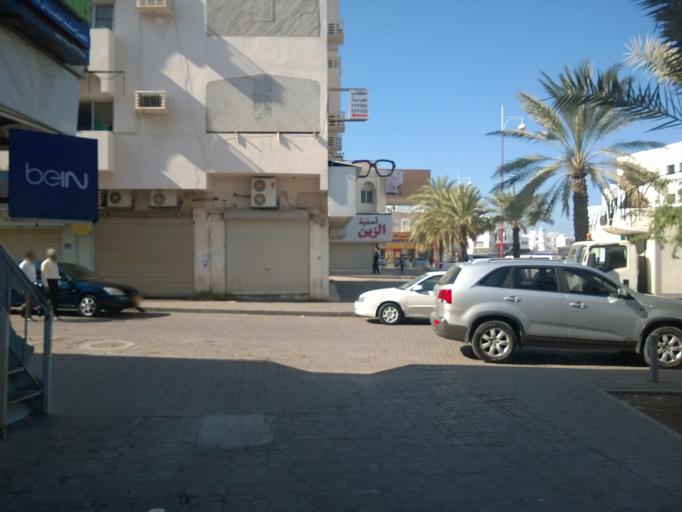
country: OM
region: Muhafazat Masqat
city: As Sib al Jadidah
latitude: 23.6790
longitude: 58.1879
